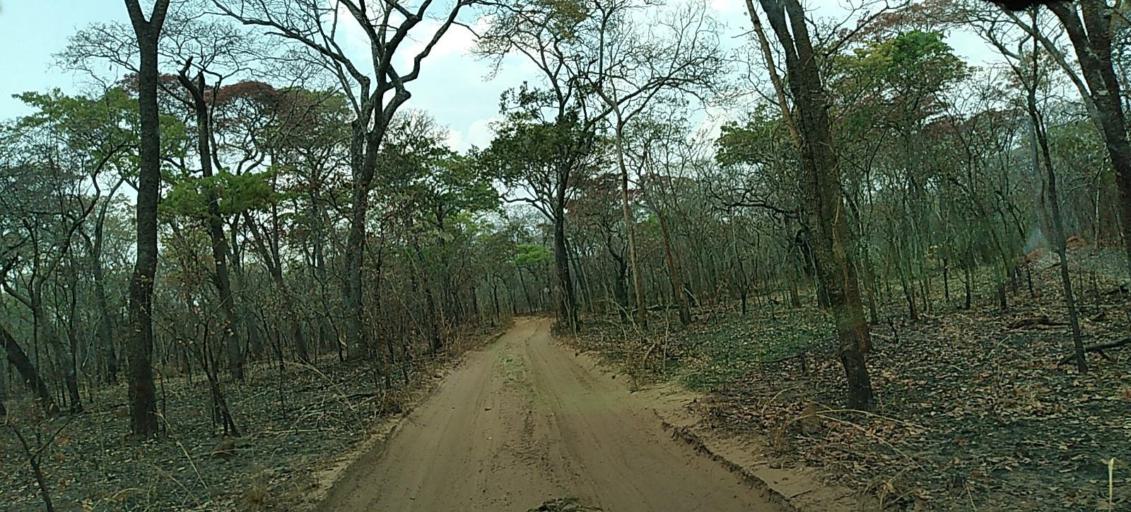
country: ZM
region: North-Western
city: Kabompo
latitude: -13.6128
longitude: 24.3745
